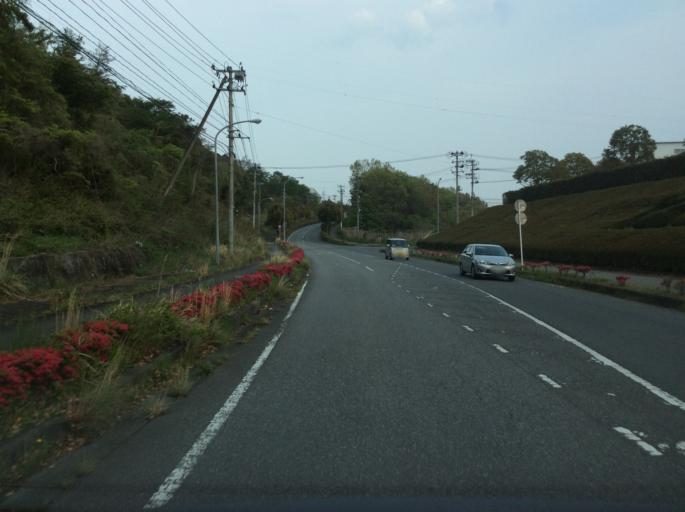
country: JP
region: Fukushima
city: Iwaki
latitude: 37.0752
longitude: 140.8569
